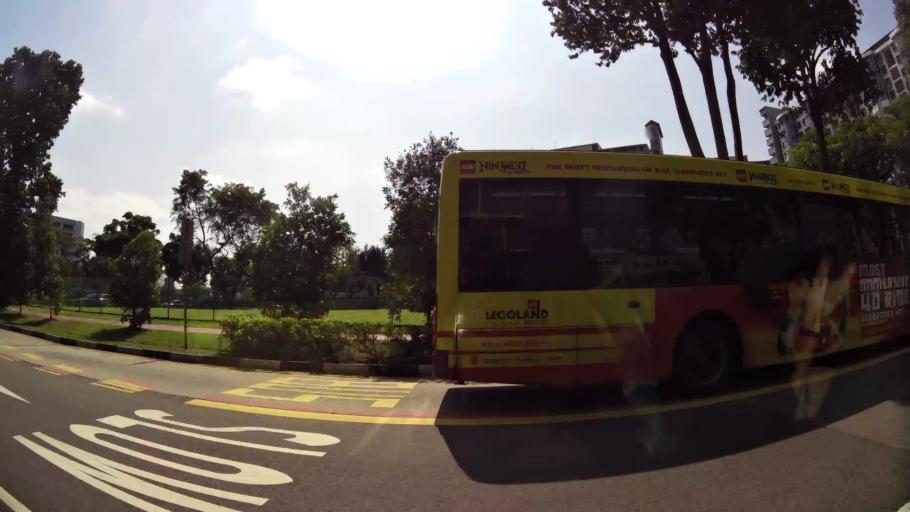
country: SG
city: Singapore
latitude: 1.3058
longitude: 103.8645
